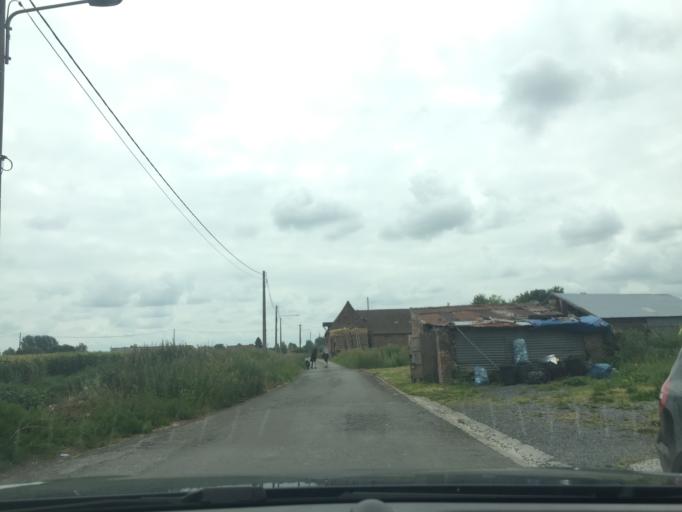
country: BE
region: Wallonia
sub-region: Province du Hainaut
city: Pecq
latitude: 50.6528
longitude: 3.2988
